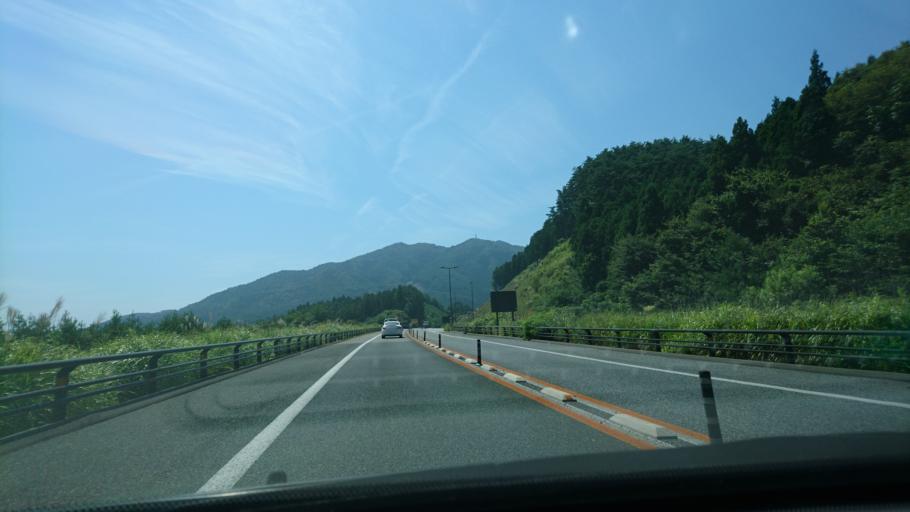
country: JP
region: Iwate
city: Ofunato
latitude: 39.0330
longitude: 141.7119
